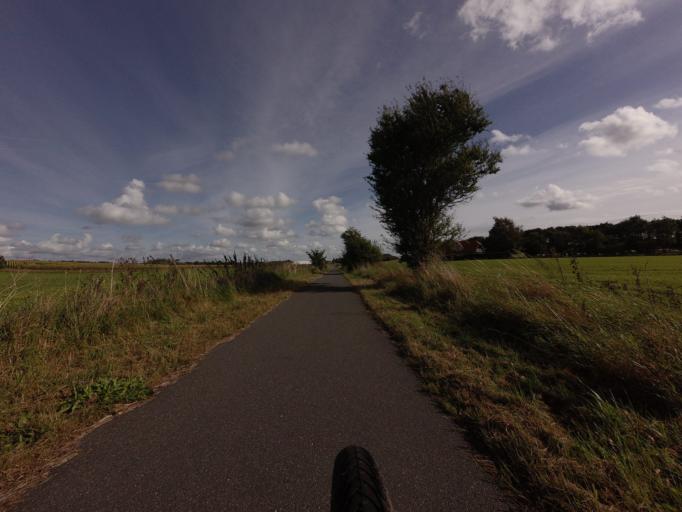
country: DK
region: Central Jutland
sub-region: Viborg Kommune
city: Bjerringbro
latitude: 56.4942
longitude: 9.6703
